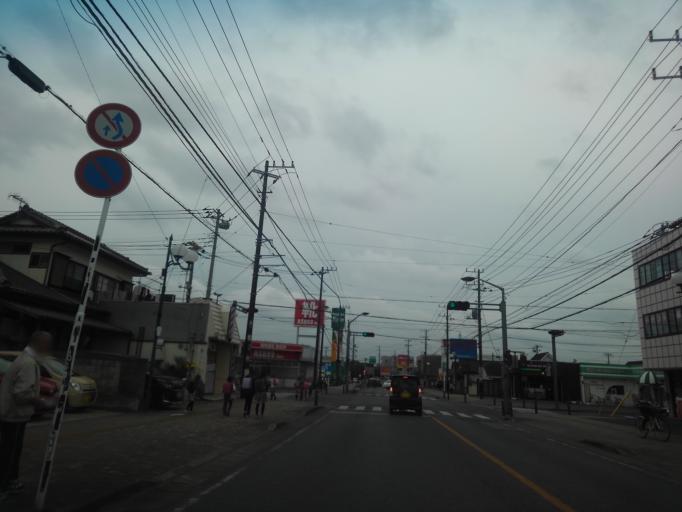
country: JP
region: Chiba
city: Kimitsu
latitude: 35.3229
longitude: 139.9188
